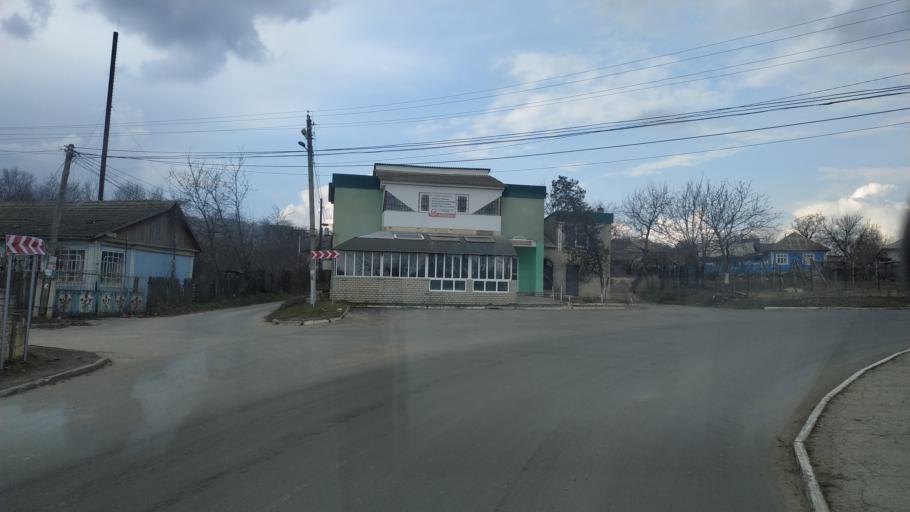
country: MD
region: Anenii Noi
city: Varnita
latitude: 46.8415
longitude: 29.3571
